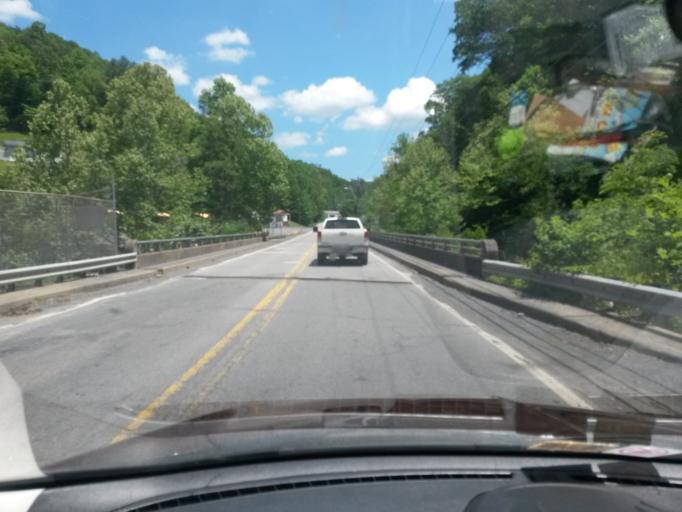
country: US
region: West Virginia
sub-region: Wyoming County
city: Pineville
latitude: 37.5858
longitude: -81.5321
